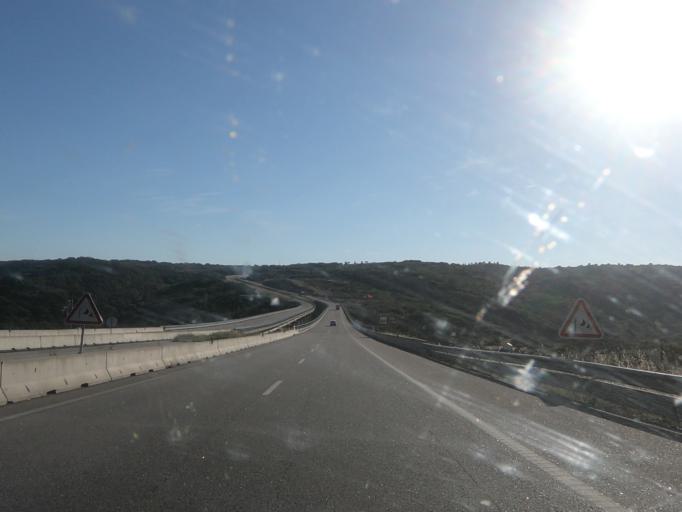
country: ES
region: Castille and Leon
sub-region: Provincia de Salamanca
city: Fuentes de Onoro
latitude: 40.6113
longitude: -6.9147
